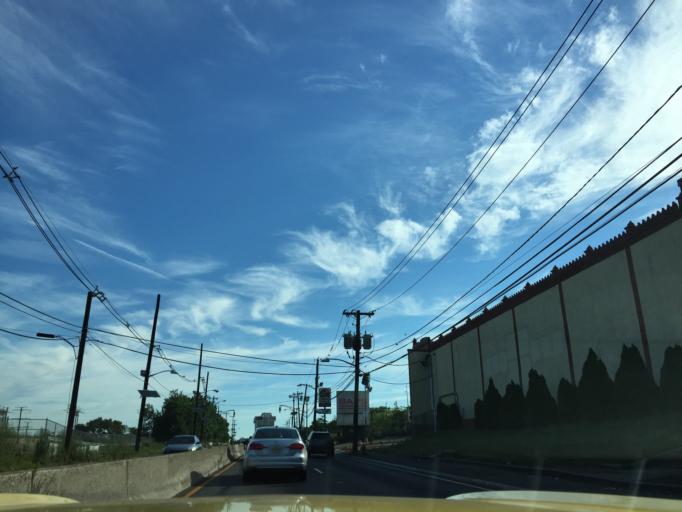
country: US
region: New Jersey
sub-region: Hudson County
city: Union City
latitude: 40.7687
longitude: -74.0449
